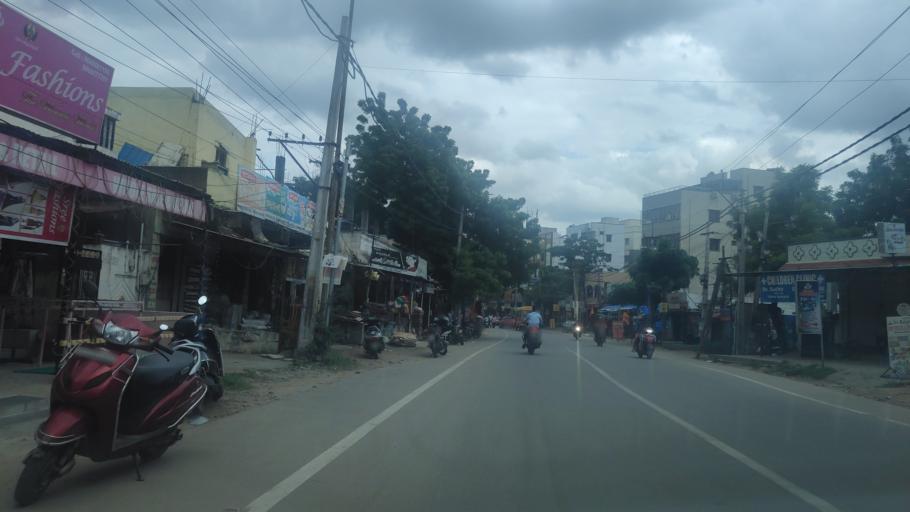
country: IN
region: Telangana
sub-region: Medak
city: Serilingampalle
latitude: 17.5061
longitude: 78.3554
